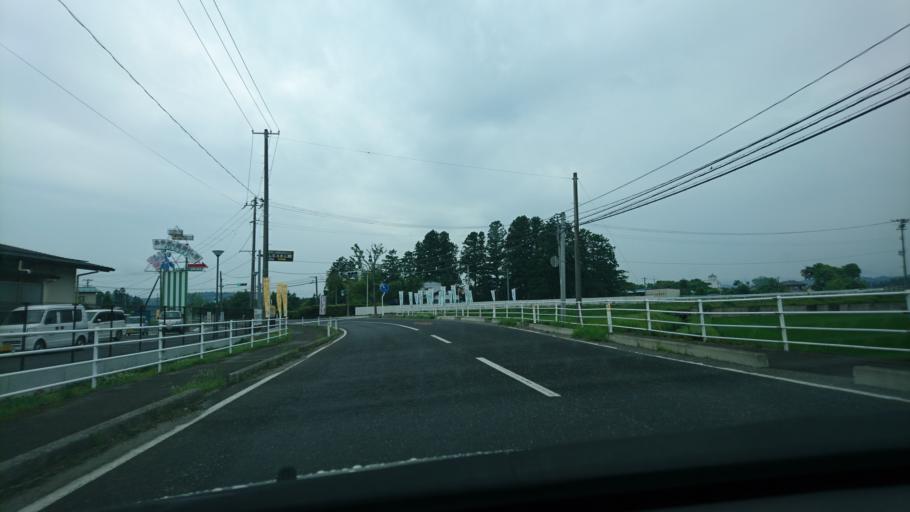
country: JP
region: Miyagi
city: Furukawa
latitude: 38.7399
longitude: 140.9475
